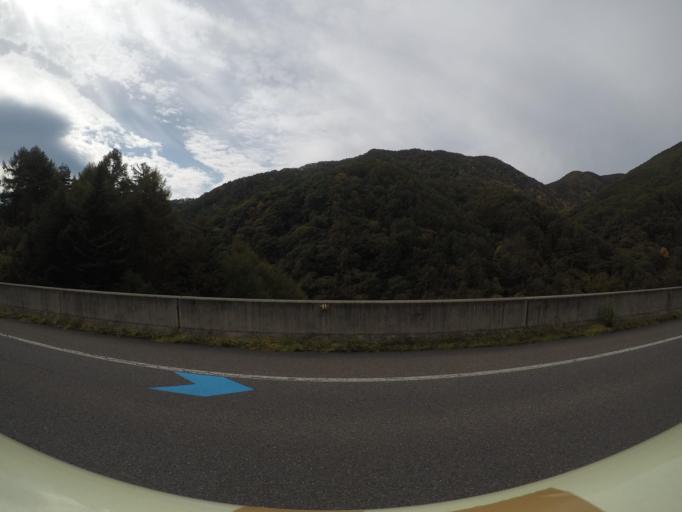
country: JP
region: Nagano
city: Ina
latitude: 35.8753
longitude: 137.8803
